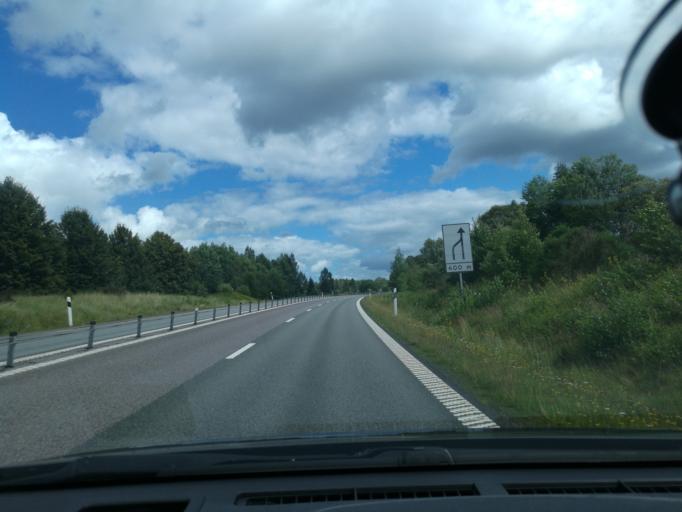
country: SE
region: Skane
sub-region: Hassleholms Kommun
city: Hastveda
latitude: 56.2454
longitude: 13.9115
